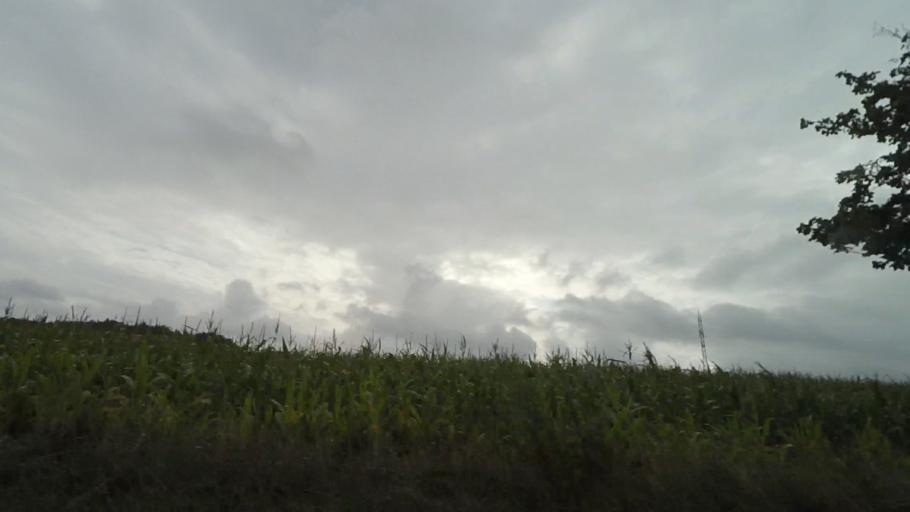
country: DK
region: Central Jutland
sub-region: Syddjurs Kommune
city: Ronde
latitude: 56.3349
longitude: 10.4570
